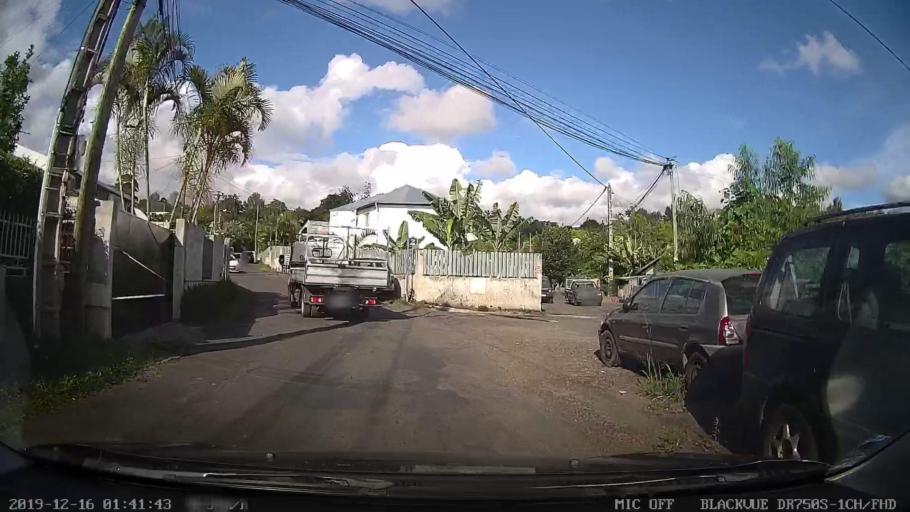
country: RE
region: Reunion
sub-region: Reunion
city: Le Tampon
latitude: -21.2552
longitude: 55.5096
